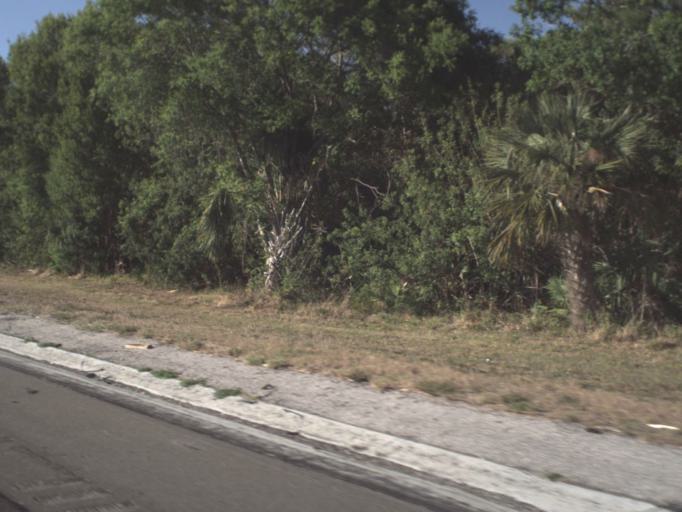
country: US
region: Florida
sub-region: Brevard County
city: Malabar
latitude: 27.9831
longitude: -80.6193
